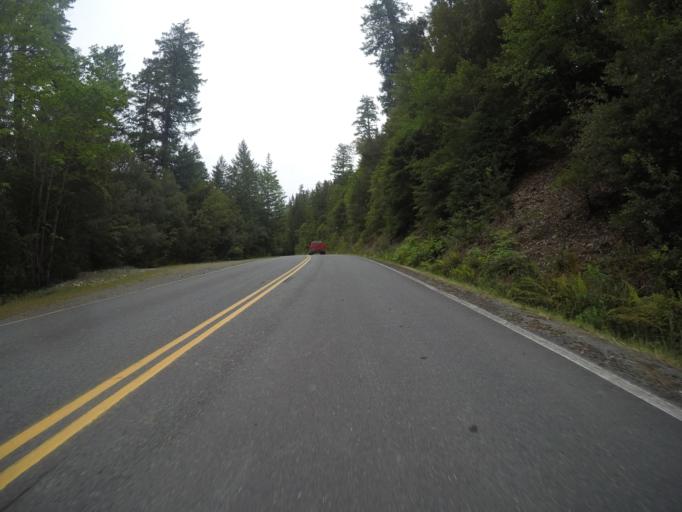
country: US
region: California
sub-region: Del Norte County
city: Bertsch-Oceanview
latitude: 41.7245
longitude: -123.9553
